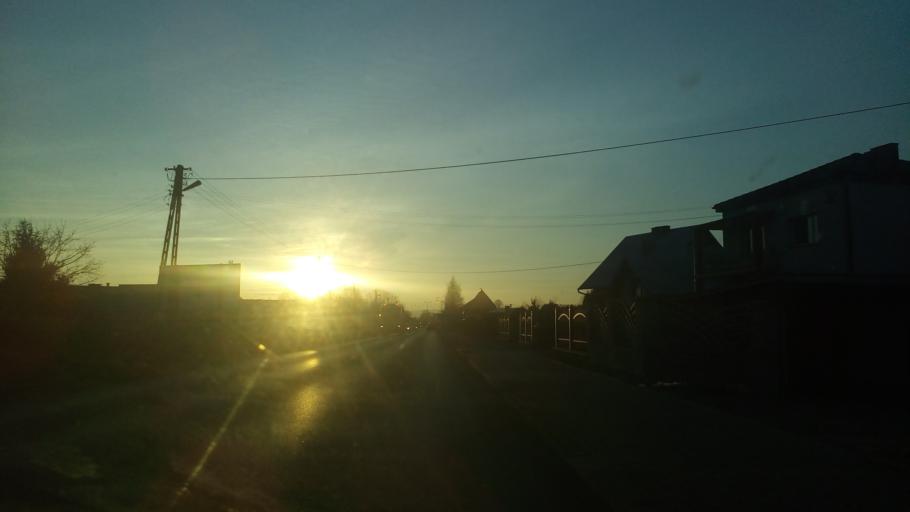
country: PL
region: Lesser Poland Voivodeship
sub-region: Powiat nowosadecki
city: Chelmiec
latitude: 49.6032
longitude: 20.6466
